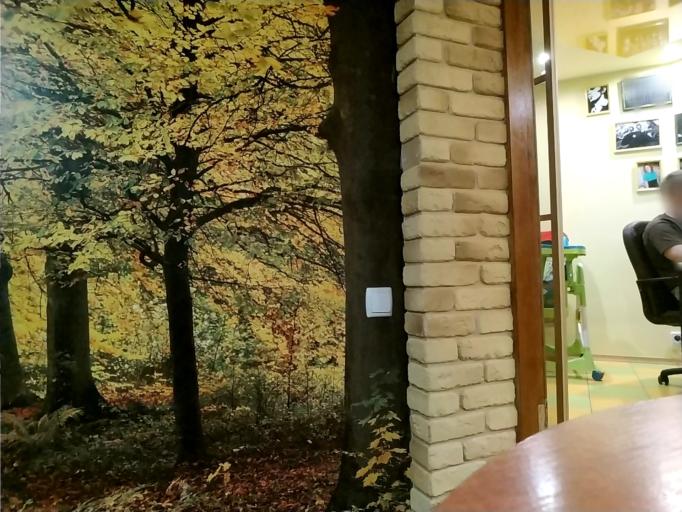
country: RU
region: Tverskaya
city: Zapadnaya Dvina
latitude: 56.3193
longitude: 31.9309
